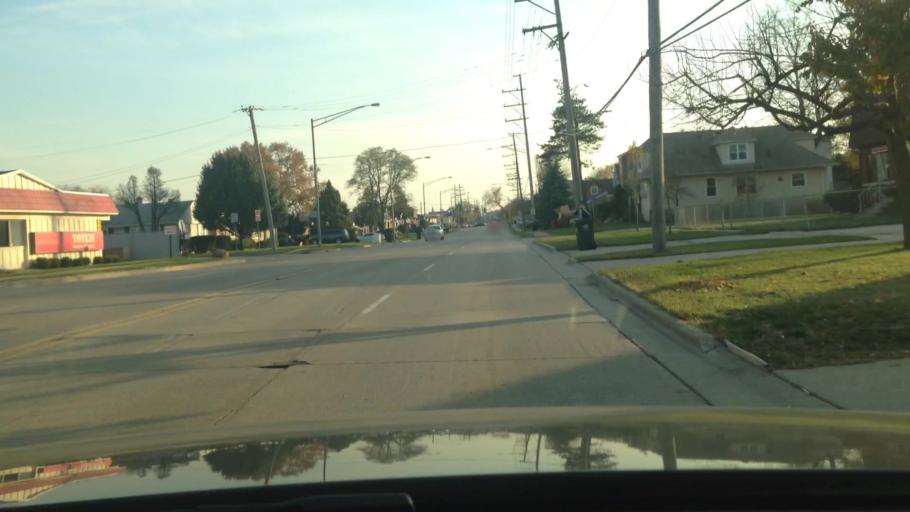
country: US
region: Illinois
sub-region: Cook County
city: Schiller Park
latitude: 41.9590
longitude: -87.8711
